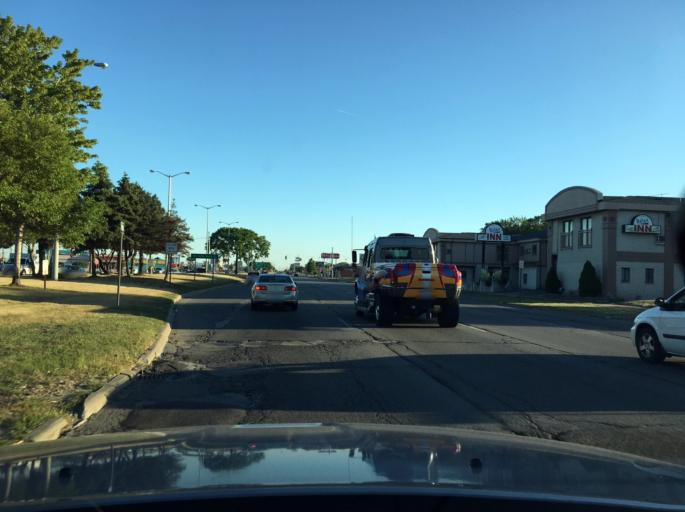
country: US
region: Michigan
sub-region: Macomb County
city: Fraser
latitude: 42.5388
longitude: -82.9098
